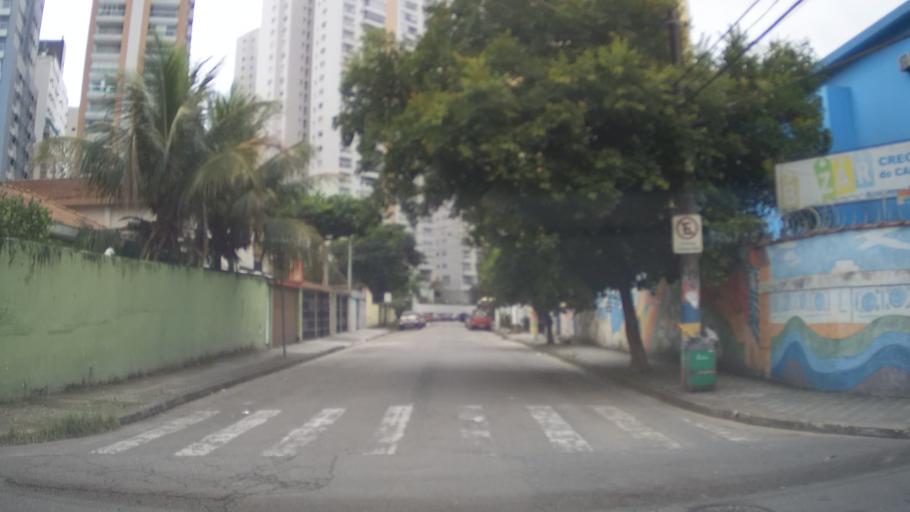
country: BR
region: Sao Paulo
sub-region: Guaruja
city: Guaruja
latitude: -23.9855
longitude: -46.2983
